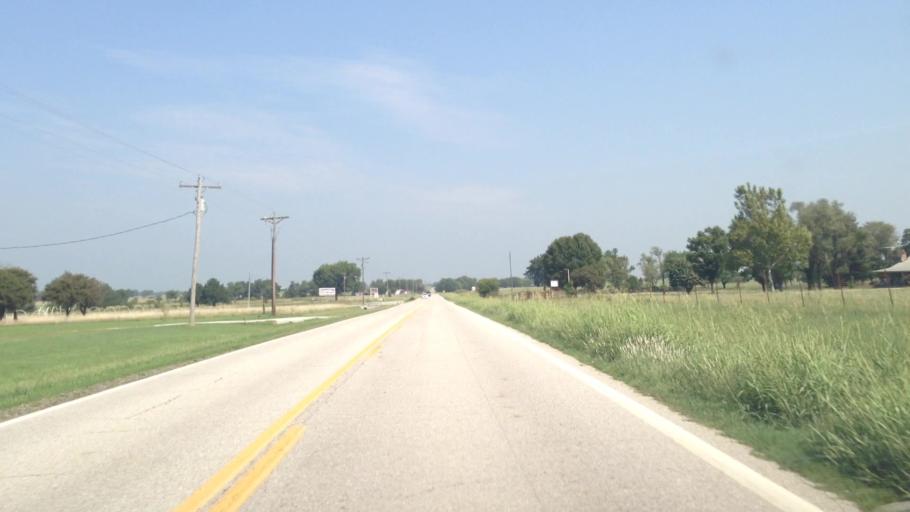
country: US
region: Oklahoma
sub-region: Craig County
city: Vinita
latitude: 36.8128
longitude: -95.1436
